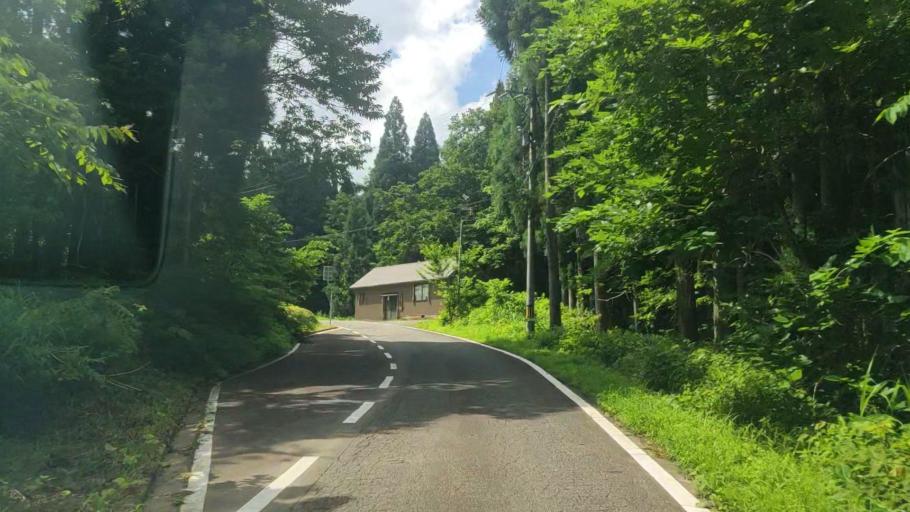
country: JP
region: Fukui
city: Katsuyama
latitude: 36.2186
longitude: 136.5303
